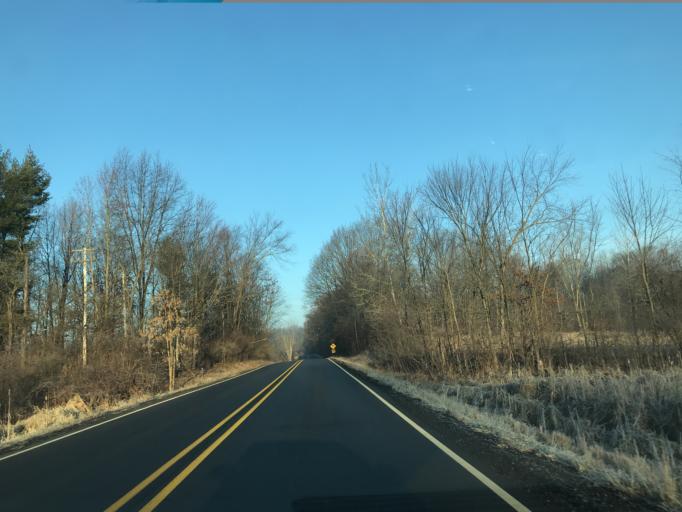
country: US
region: Michigan
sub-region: Ingham County
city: Leslie
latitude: 42.4329
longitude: -84.5349
